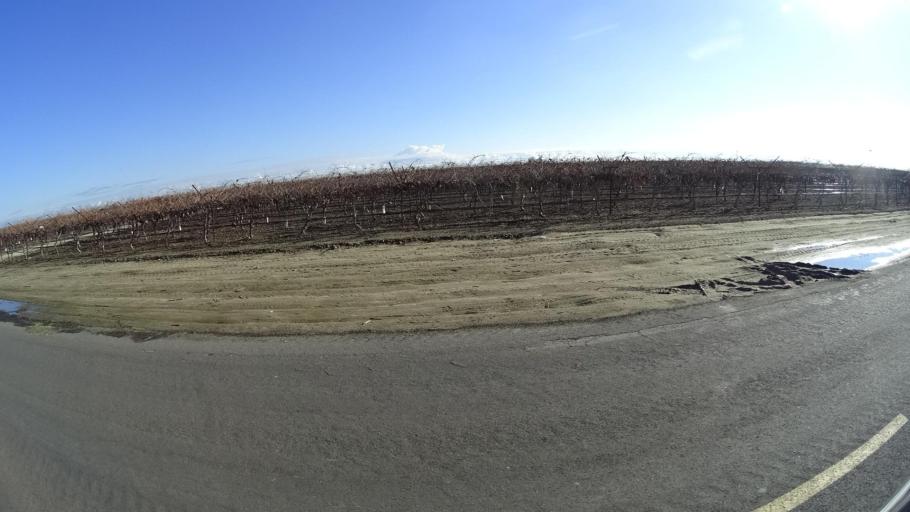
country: US
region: California
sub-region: Kern County
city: McFarland
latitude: 35.6904
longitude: -119.2764
